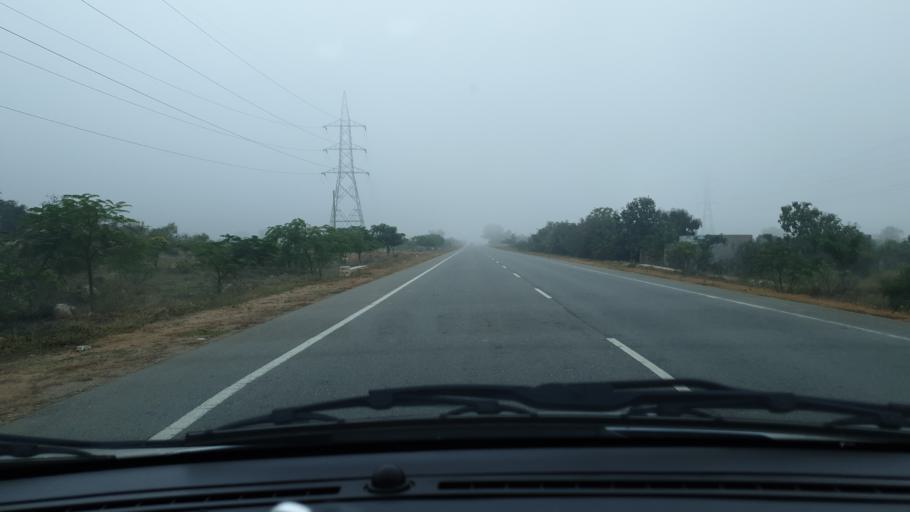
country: IN
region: Telangana
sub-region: Nalgonda
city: Devarkonda
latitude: 16.6259
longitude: 78.6668
